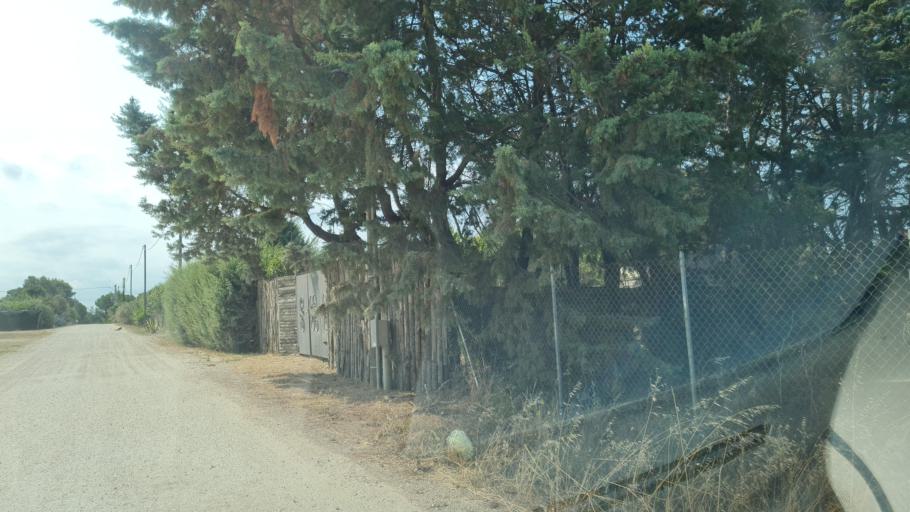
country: IT
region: Latium
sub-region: Provincia di Viterbo
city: Tarquinia
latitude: 42.1939
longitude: 11.7291
